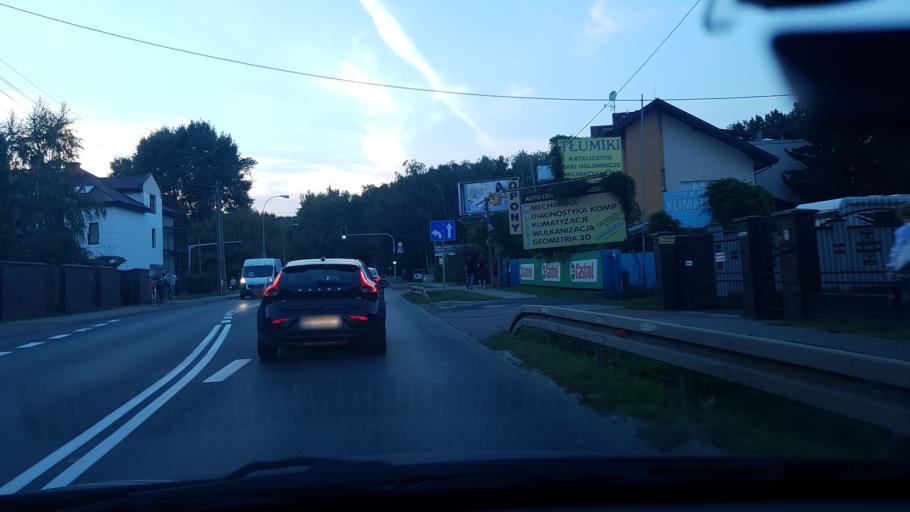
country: PL
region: Masovian Voivodeship
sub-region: Warszawa
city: Targowek
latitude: 52.2909
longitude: 21.0696
